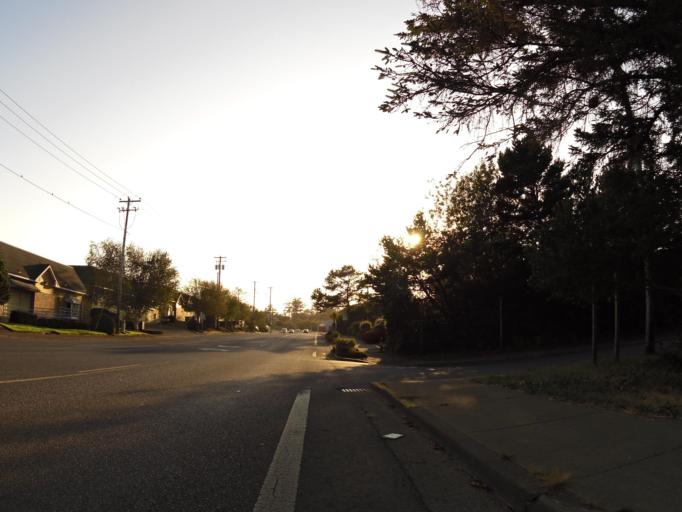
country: US
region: Oregon
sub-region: Lincoln County
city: Lincoln City
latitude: 44.9598
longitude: -124.0110
